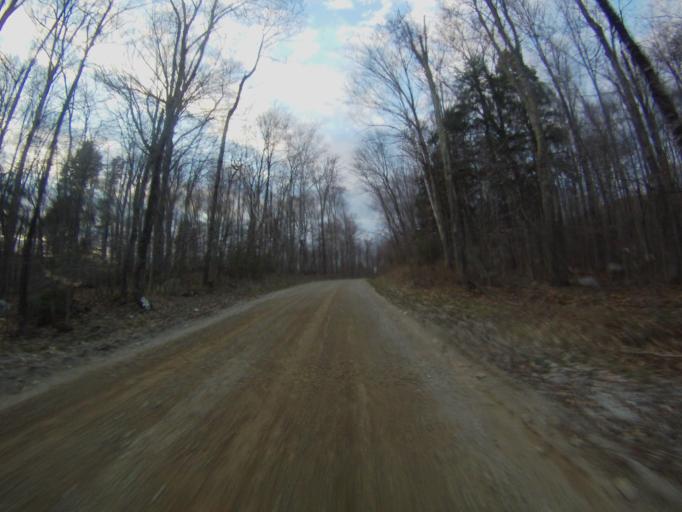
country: US
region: Vermont
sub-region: Rutland County
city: Brandon
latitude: 43.9188
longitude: -73.0183
